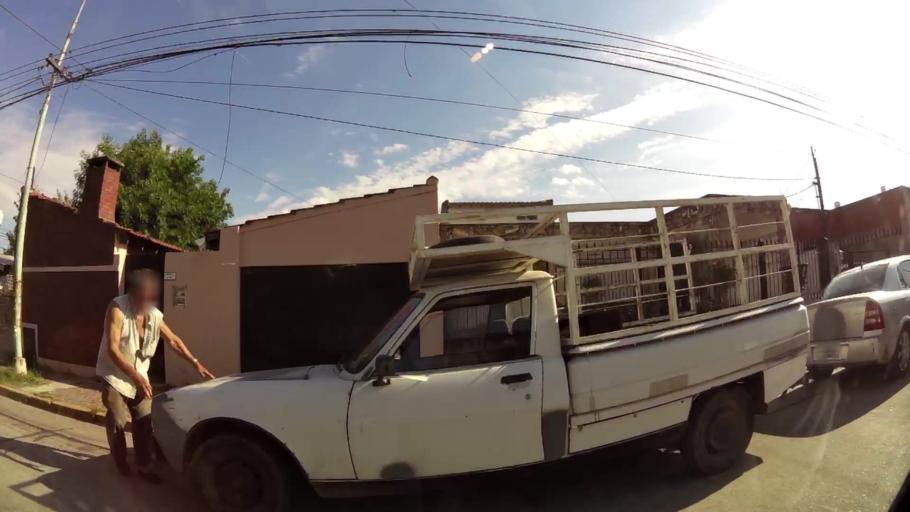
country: AR
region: Buenos Aires
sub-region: Partido de Merlo
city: Merlo
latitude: -34.6568
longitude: -58.7233
